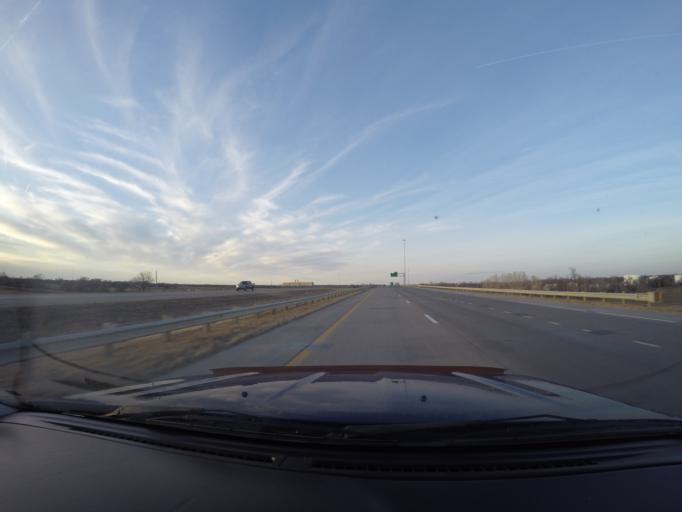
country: US
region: Kansas
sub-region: Saline County
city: Salina
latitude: 38.8377
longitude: -97.6445
